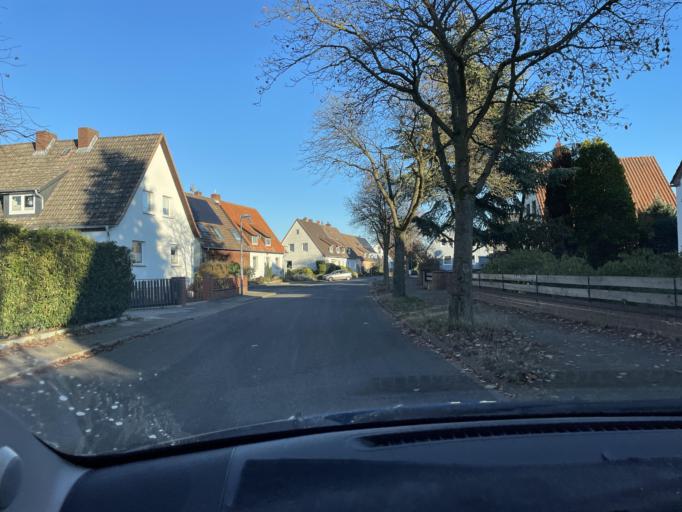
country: DE
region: Lower Saxony
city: Adendorf
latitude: 53.2637
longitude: 10.4329
